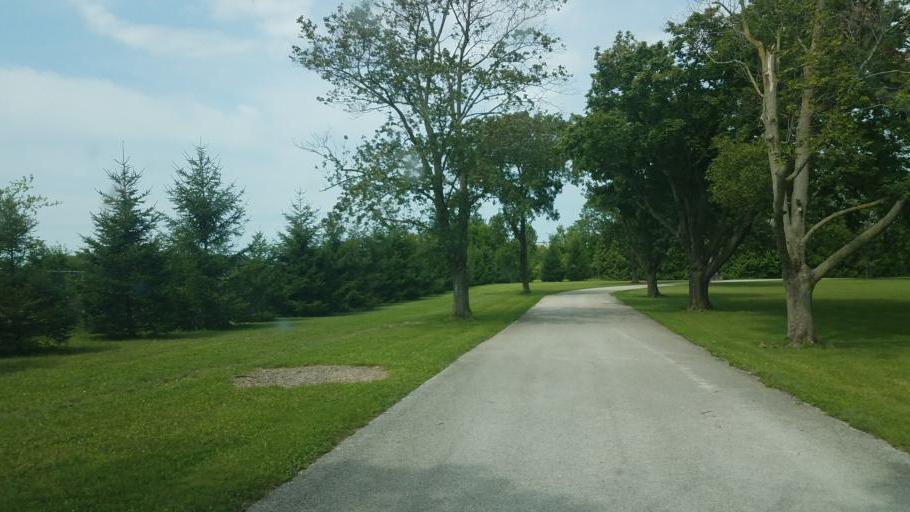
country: US
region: Ohio
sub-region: Wyandot County
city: Carey
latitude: 40.9492
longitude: -83.3948
